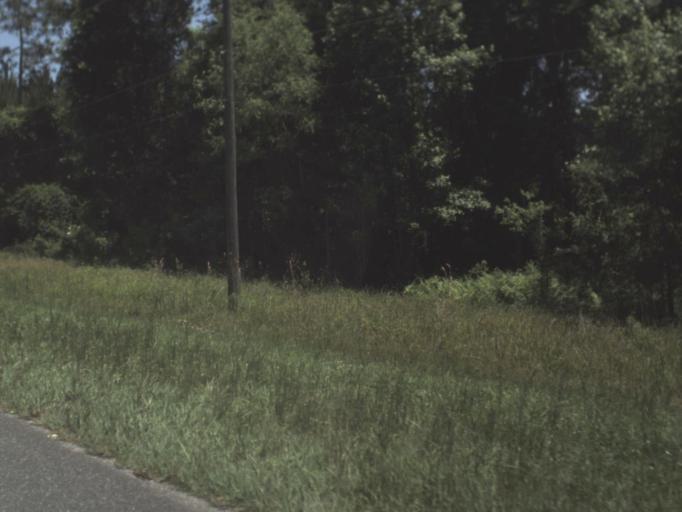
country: US
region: Florida
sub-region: Columbia County
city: Watertown
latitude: 30.1924
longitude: -82.5178
